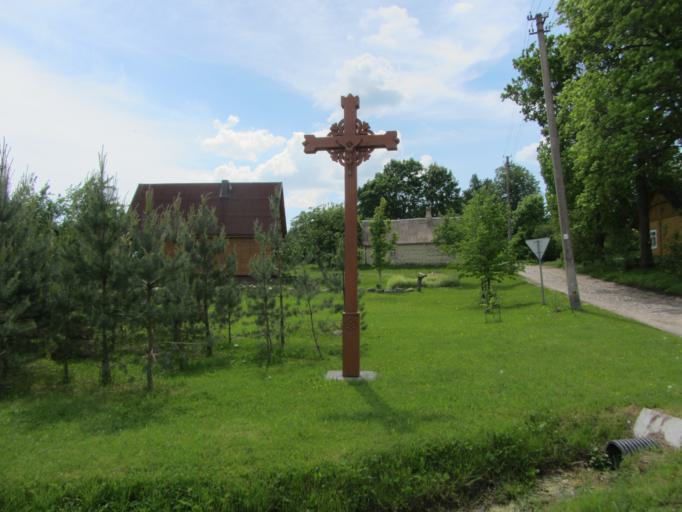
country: LT
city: Pabrade
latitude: 55.0720
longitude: 25.6639
